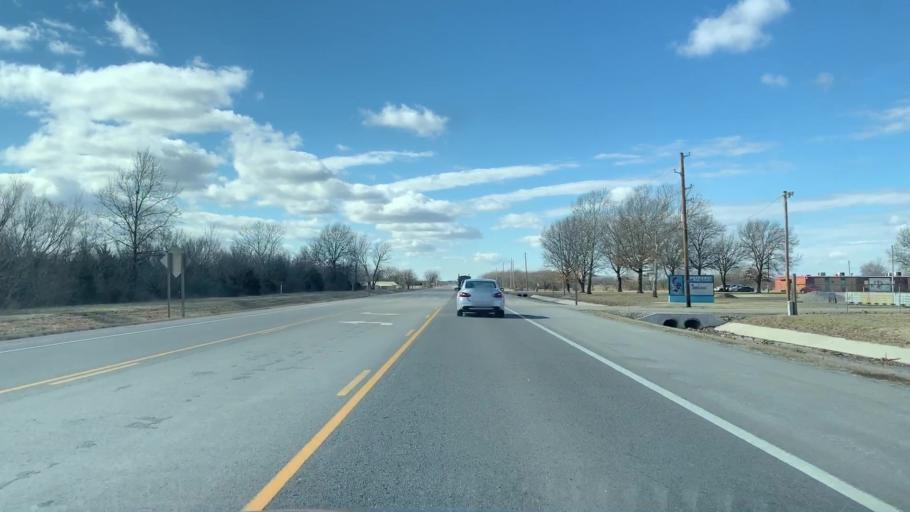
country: US
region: Kansas
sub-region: Crawford County
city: Pittsburg
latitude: 37.3395
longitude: -94.8353
